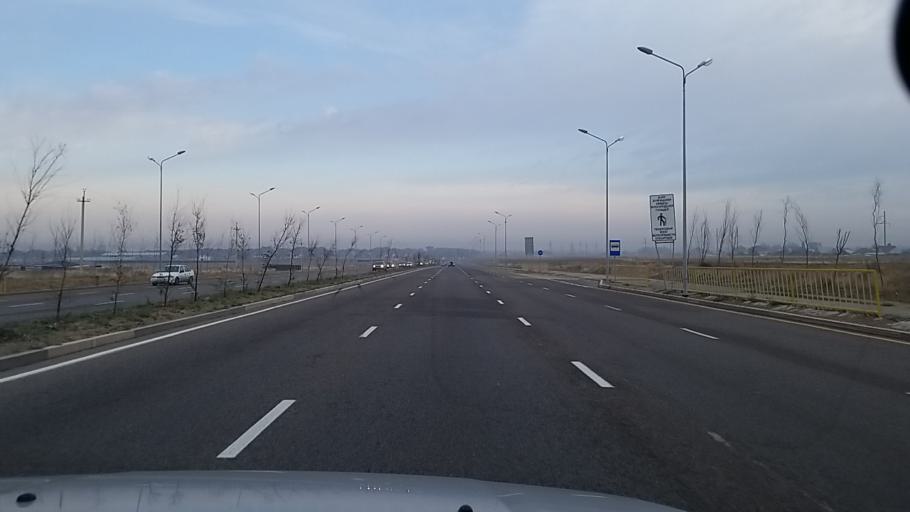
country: KZ
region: Almaty Oblysy
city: Burunday
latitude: 43.3414
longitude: 76.8339
